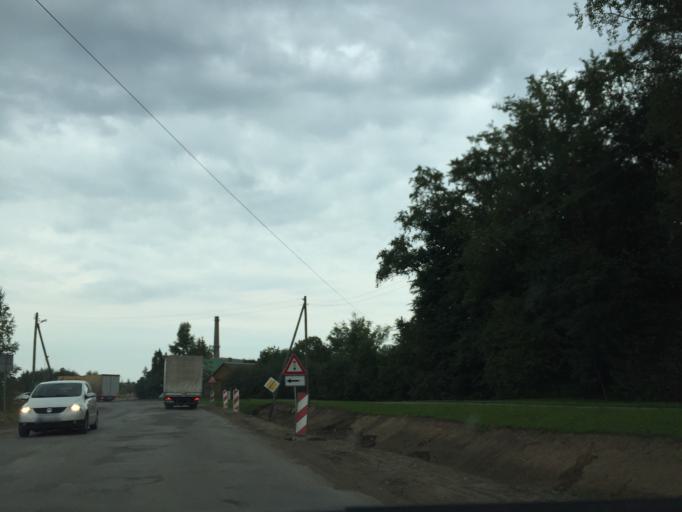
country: LV
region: Ludzas Rajons
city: Ludza
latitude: 56.5367
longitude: 27.6981
